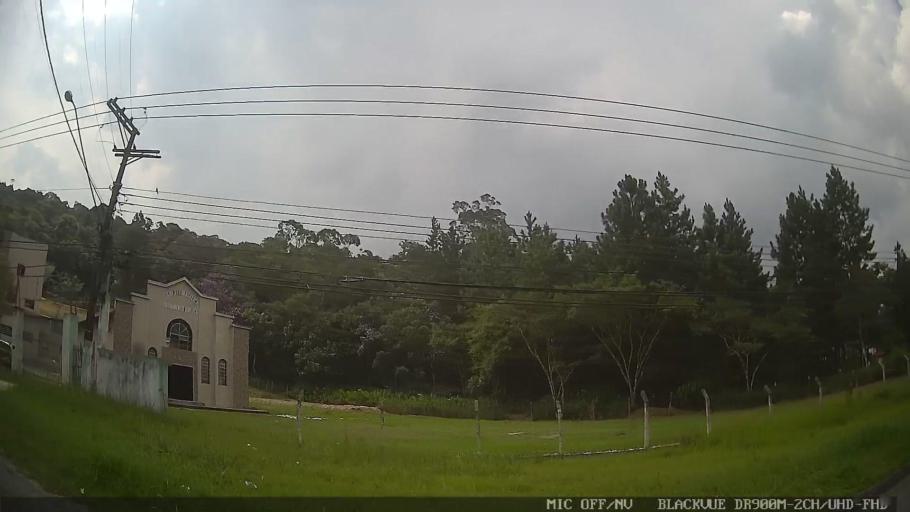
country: BR
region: Sao Paulo
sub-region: Ribeirao Pires
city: Ribeirao Pires
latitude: -23.6626
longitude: -46.3787
